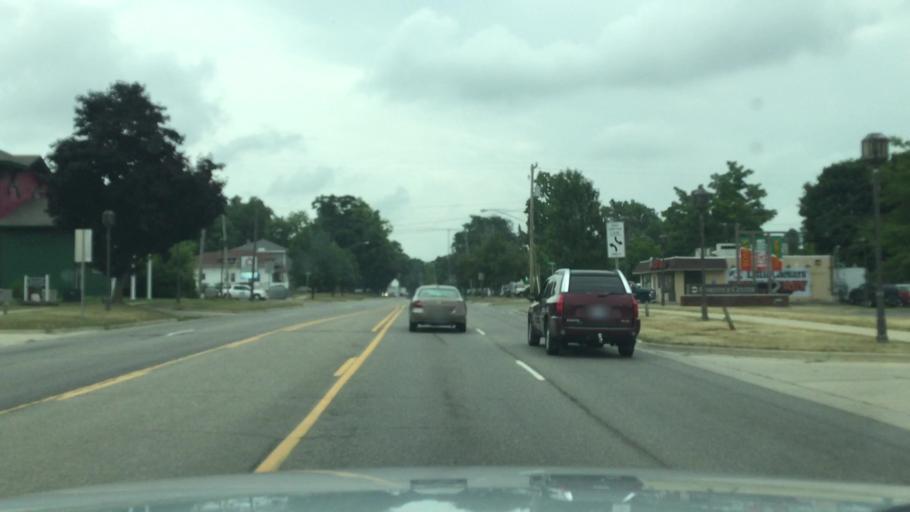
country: US
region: Michigan
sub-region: Shiawassee County
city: Owosso
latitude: 42.9975
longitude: -84.1679
